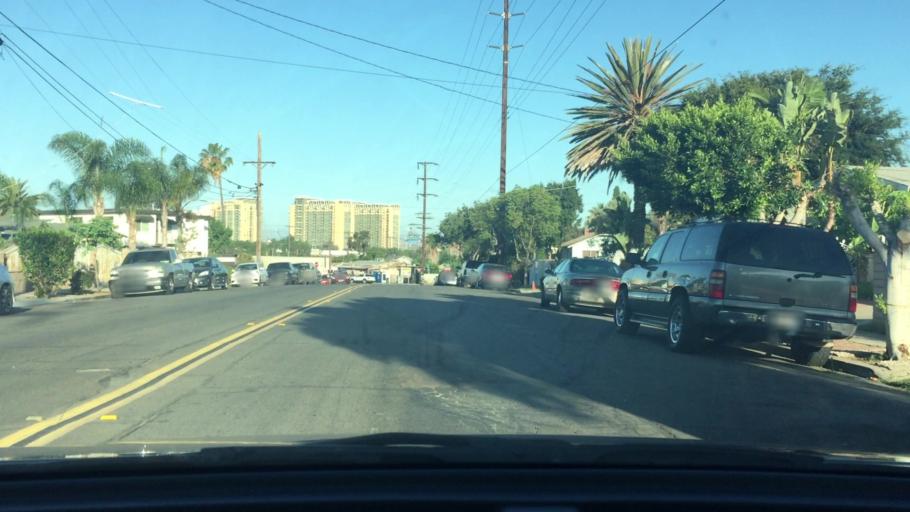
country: US
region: California
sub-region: San Diego County
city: National City
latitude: 32.6887
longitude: -117.1107
